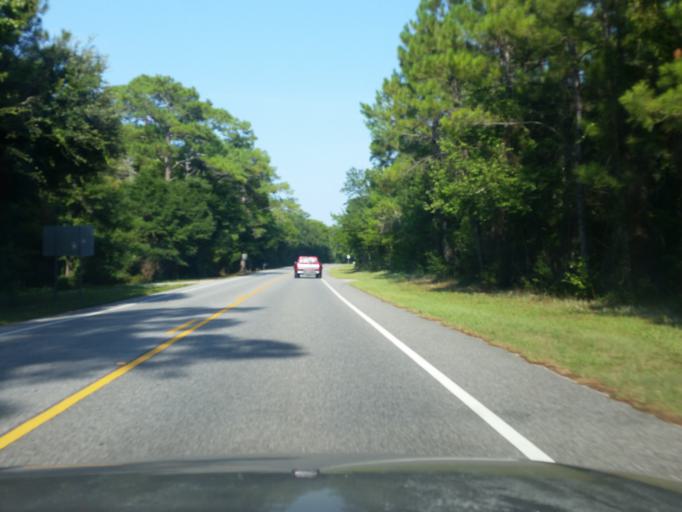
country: US
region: Alabama
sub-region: Baldwin County
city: Gulf Shores
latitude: 30.2520
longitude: -87.8078
